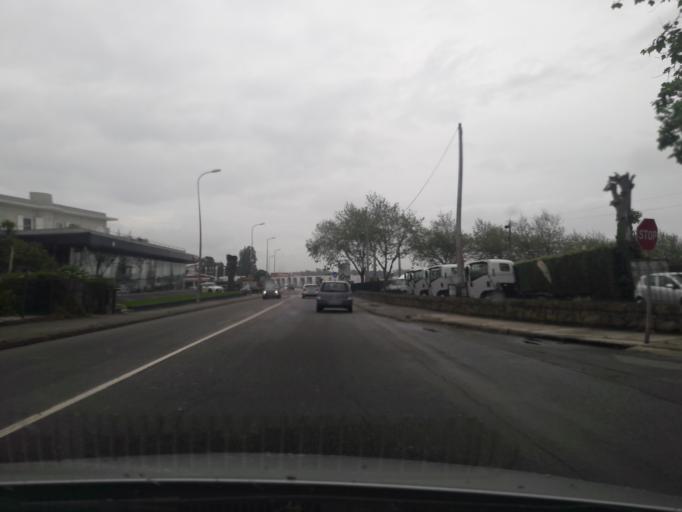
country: PT
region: Porto
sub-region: Vila do Conde
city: Vila do Conde
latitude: 41.3442
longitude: -8.7366
